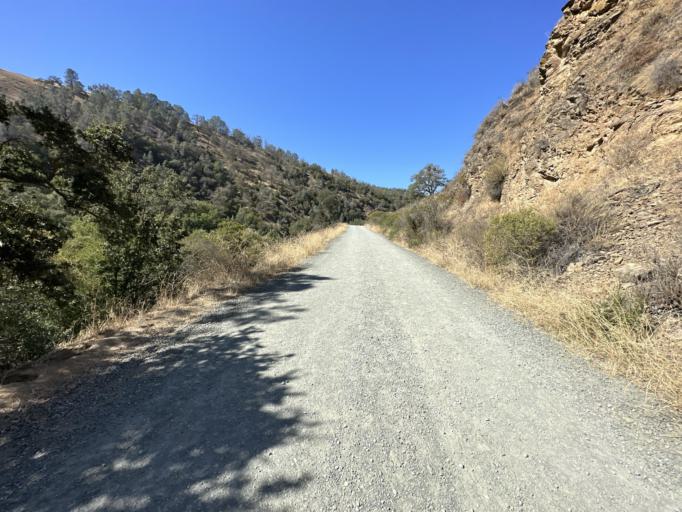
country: US
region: California
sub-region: Santa Clara County
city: Milpitas
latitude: 37.5049
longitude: -121.8256
